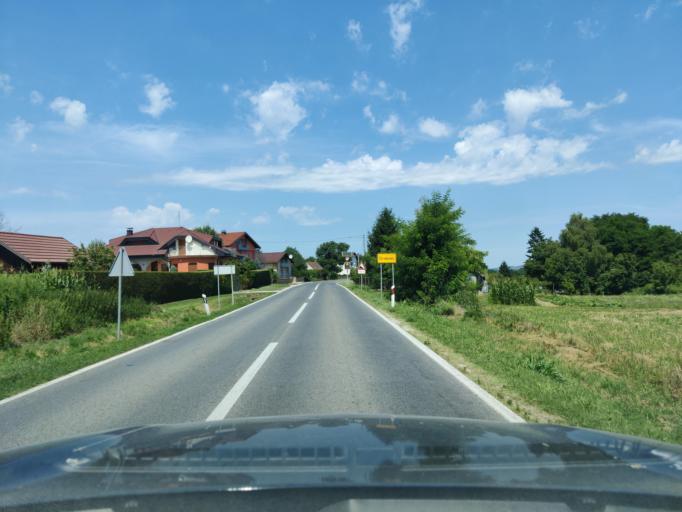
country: HR
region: Medimurska
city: Vratisinec
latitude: 46.4671
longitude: 16.4255
